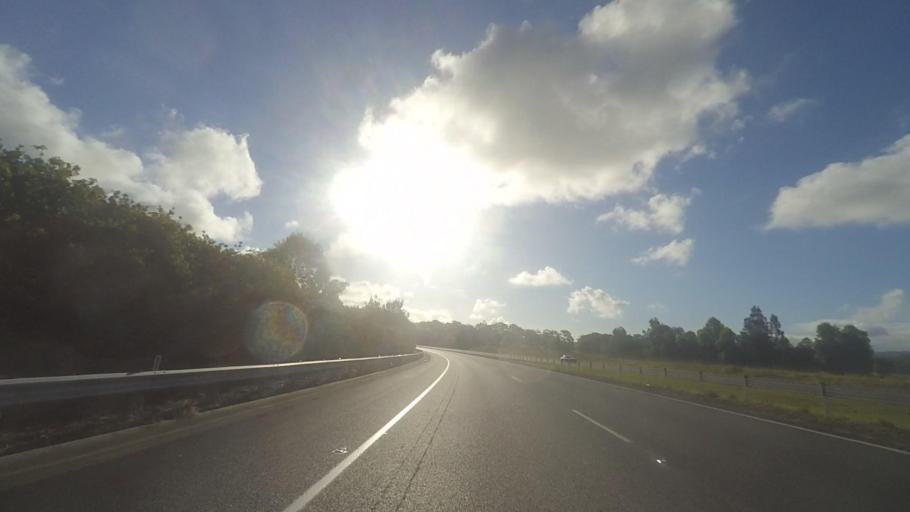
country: AU
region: New South Wales
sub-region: Great Lakes
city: Nabiac
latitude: -32.0924
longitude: 152.3882
